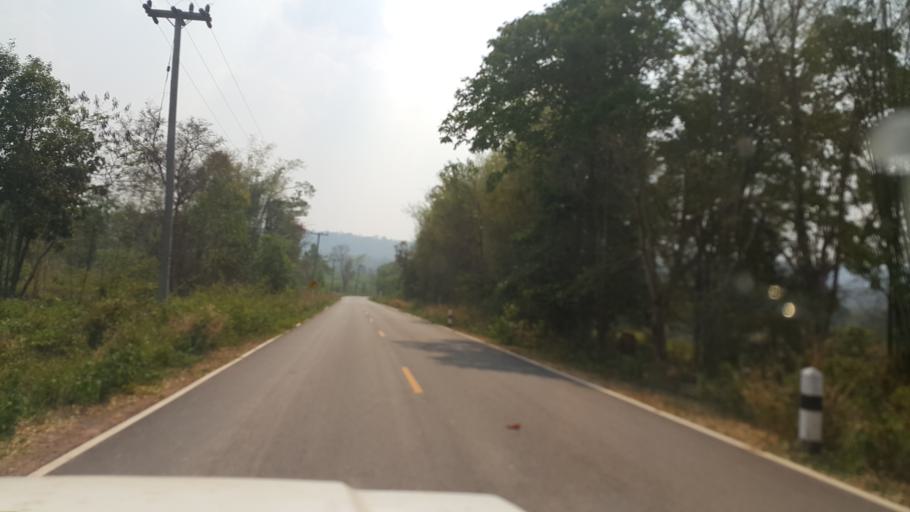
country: TH
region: Nakhon Phanom
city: Ban Phaeng
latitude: 17.9539
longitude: 104.1728
